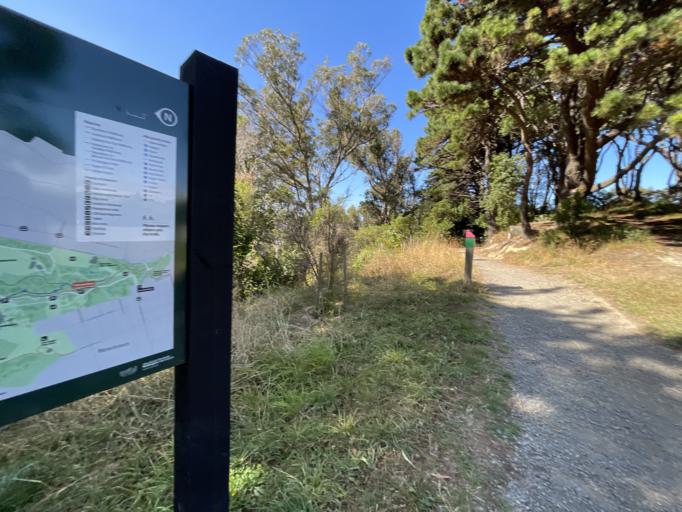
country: NZ
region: Wellington
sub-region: Wellington City
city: Wellington
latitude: -41.3096
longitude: 174.7883
